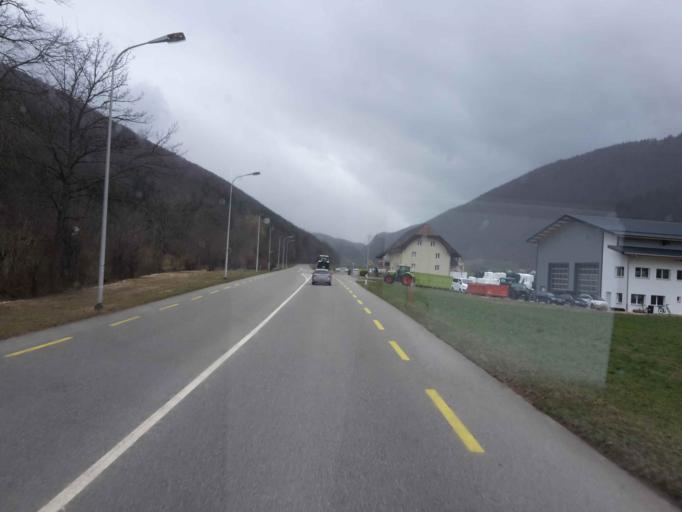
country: CH
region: Solothurn
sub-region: Bezirk Thal
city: Matzendorf
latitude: 47.2938
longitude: 7.5943
